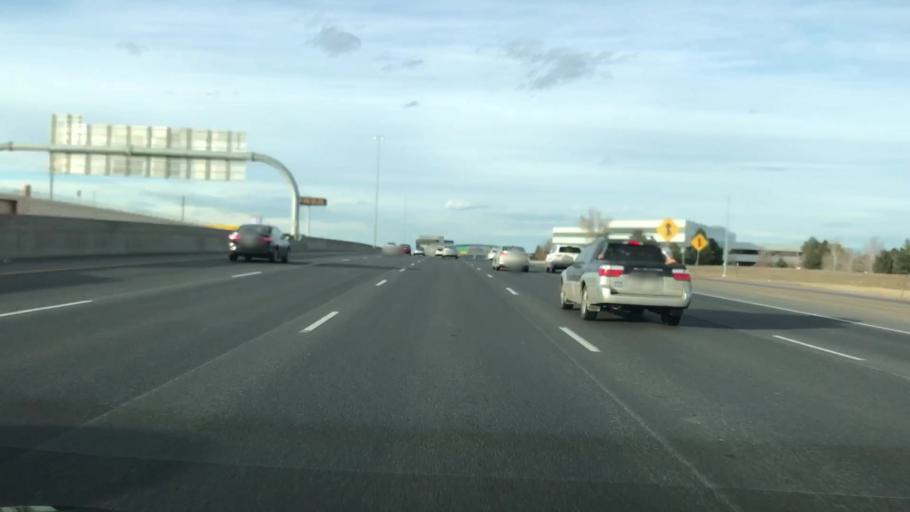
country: US
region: Colorado
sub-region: Arapahoe County
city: Centennial
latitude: 39.5672
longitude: -104.8708
